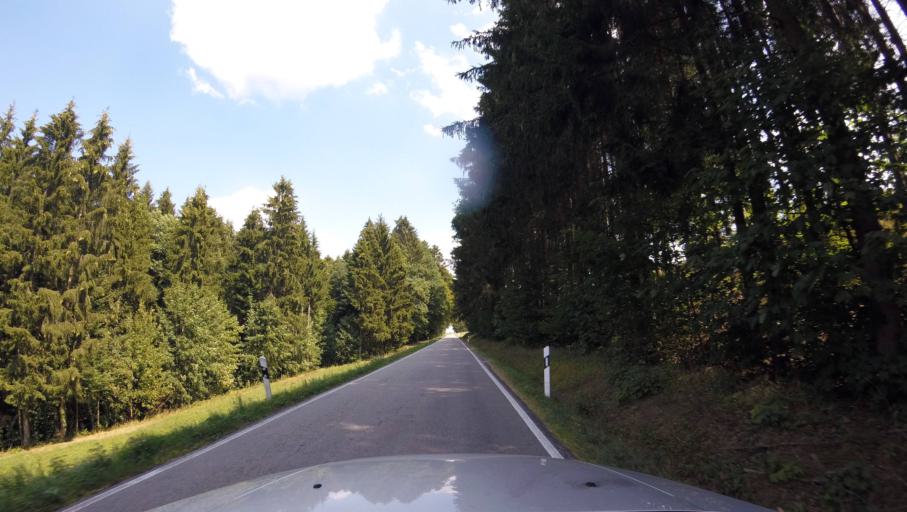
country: DE
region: Baden-Wuerttemberg
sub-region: Regierungsbezirk Stuttgart
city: Kaisersbach
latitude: 48.9489
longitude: 9.6007
